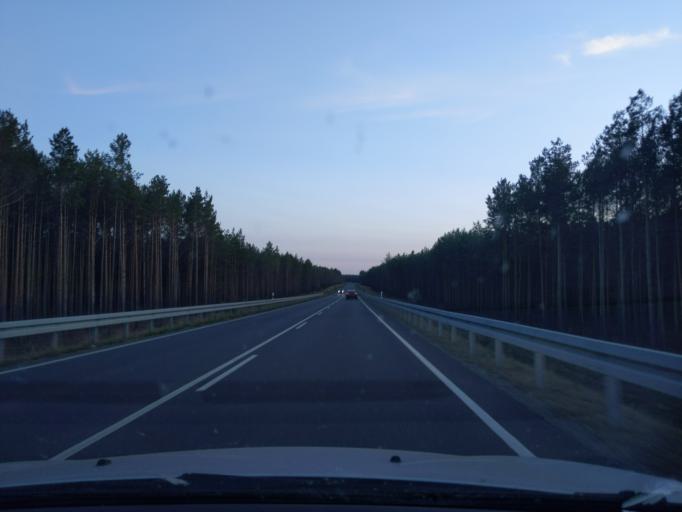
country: DE
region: Saxony
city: Hoyerswerda
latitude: 51.4219
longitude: 14.2956
